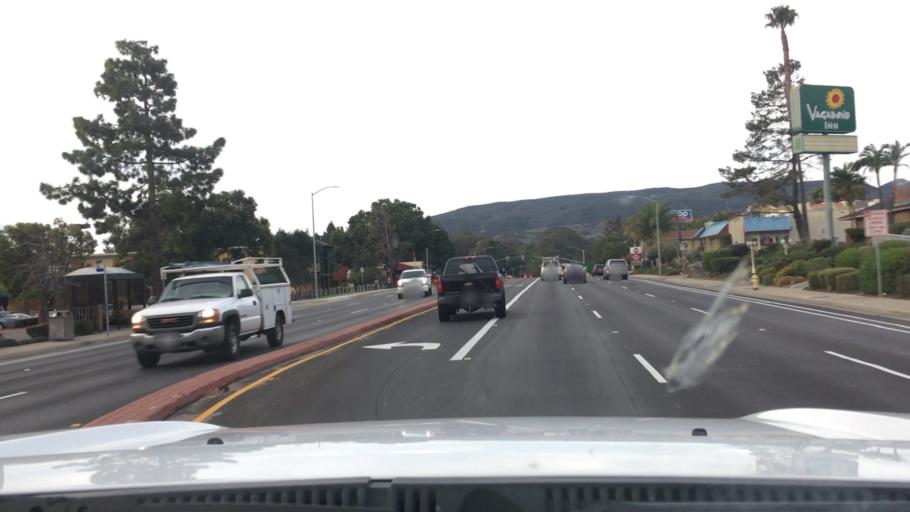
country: US
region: California
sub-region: San Luis Obispo County
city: San Luis Obispo
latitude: 35.2642
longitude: -120.6762
